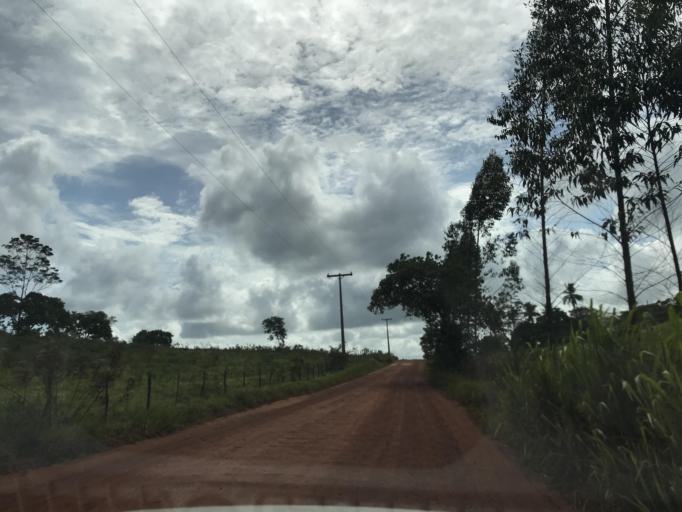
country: BR
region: Bahia
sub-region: Entre Rios
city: Entre Rios
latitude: -12.1665
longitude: -38.1569
